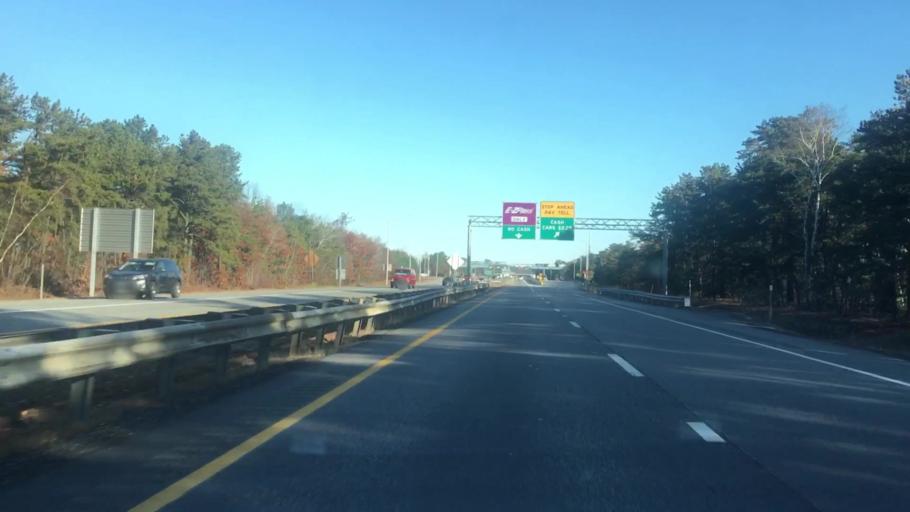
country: US
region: Maine
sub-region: Cumberland County
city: New Gloucester
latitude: 43.9319
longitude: -70.3356
